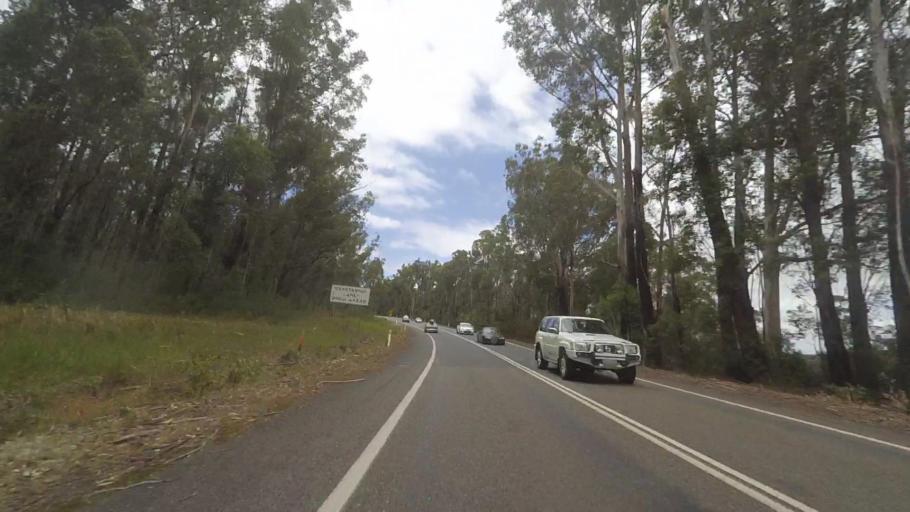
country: AU
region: New South Wales
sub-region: Shoalhaven Shire
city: Milton
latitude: -35.1361
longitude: 150.4645
